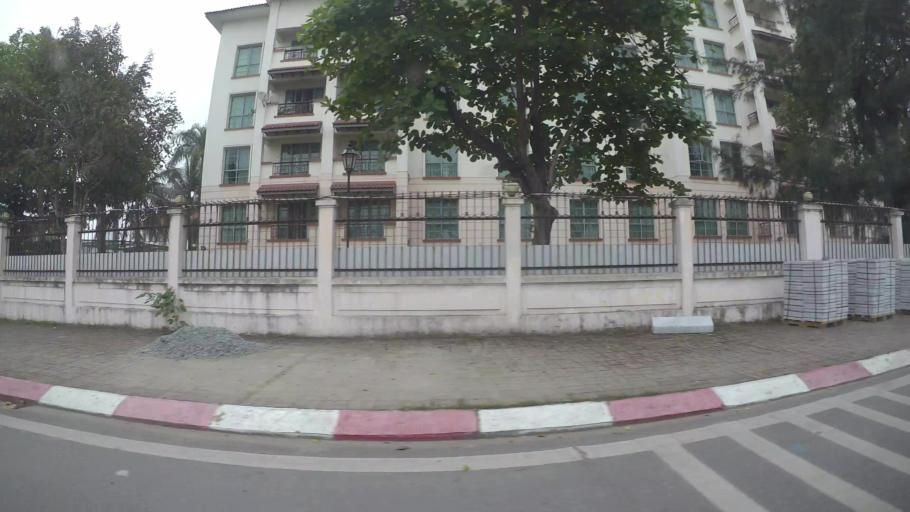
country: VN
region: Ha Noi
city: Tay Ho
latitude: 21.0659
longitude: 105.8205
